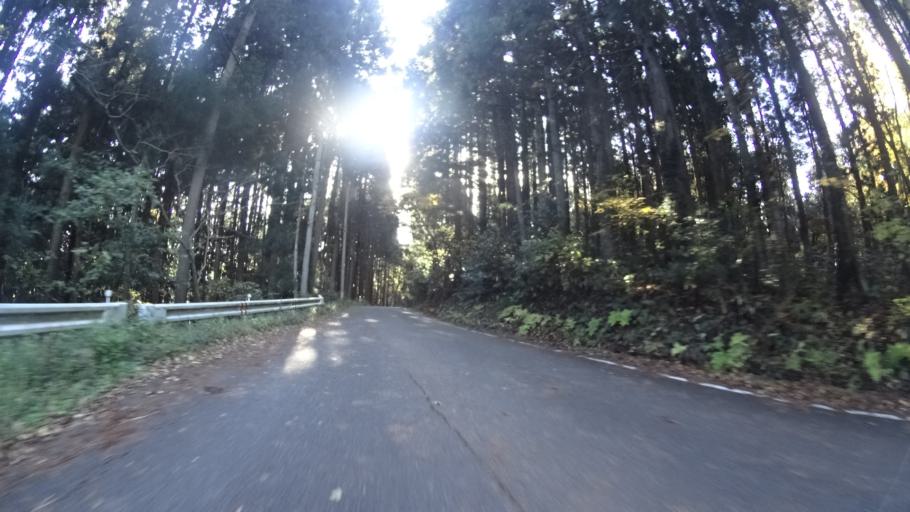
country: JP
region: Niigata
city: Yoshida-kasugacho
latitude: 37.6601
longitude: 138.8129
